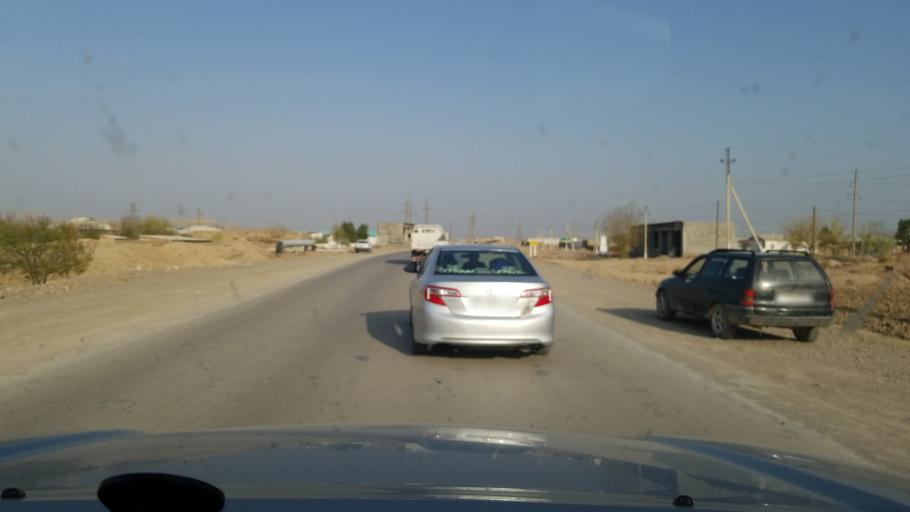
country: AF
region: Jowzjan
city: Qarqin
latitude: 37.5165
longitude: 66.0336
